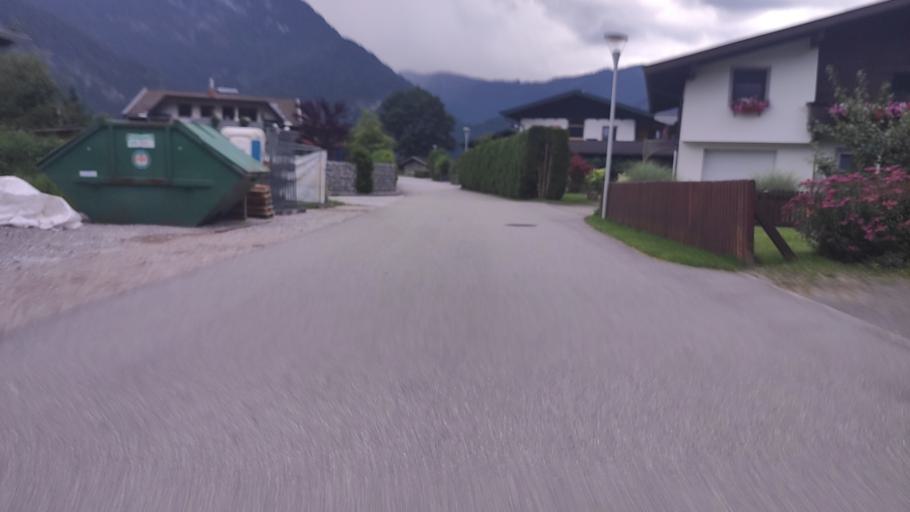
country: AT
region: Salzburg
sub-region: Politischer Bezirk Zell am See
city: Sankt Martin bei Lofer
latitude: 47.5724
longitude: 12.6958
